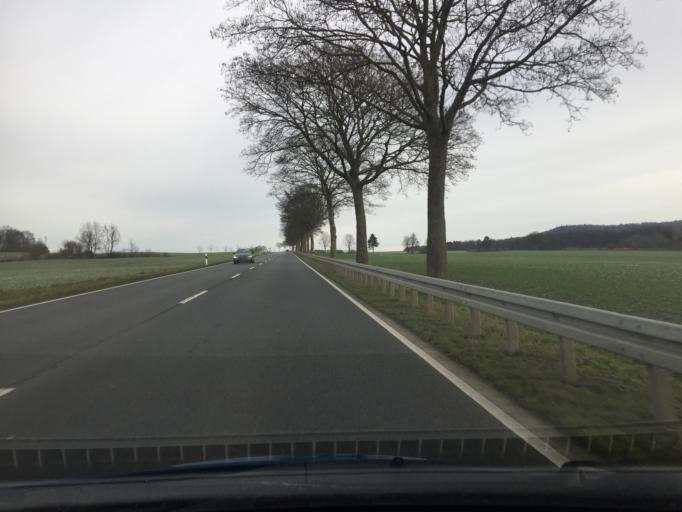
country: DE
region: Lower Saxony
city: Holenberg
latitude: 51.9031
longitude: 9.6014
